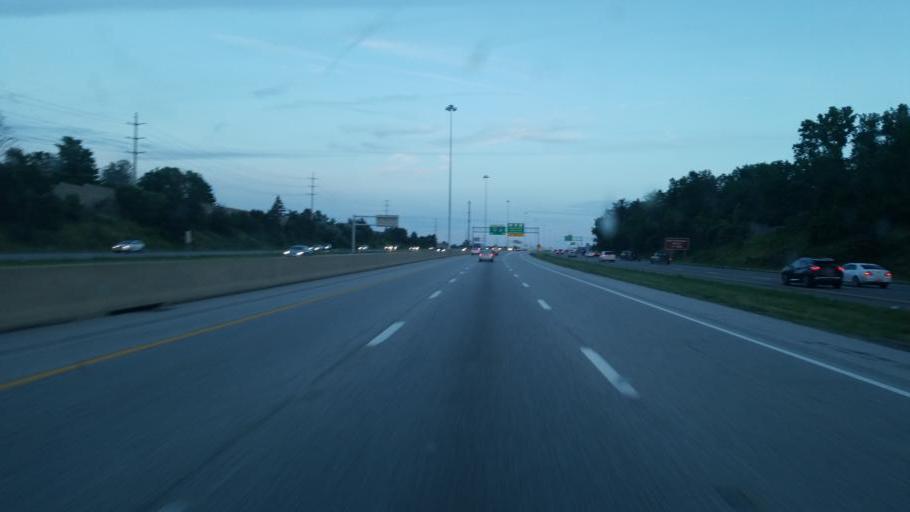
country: US
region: Ohio
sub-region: Cuyahoga County
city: Pepper Pike
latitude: 41.4854
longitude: -81.4868
